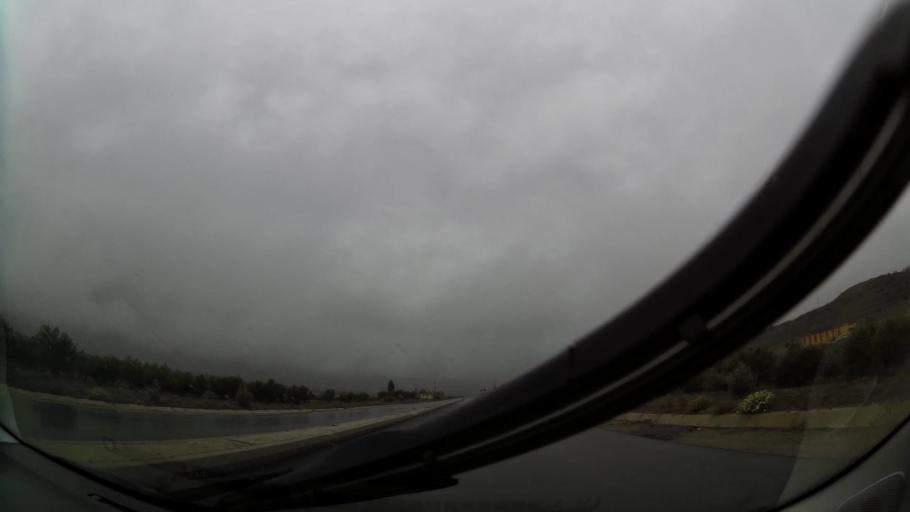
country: MA
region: Oriental
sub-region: Nador
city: Midar
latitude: 34.8342
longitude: -3.7201
